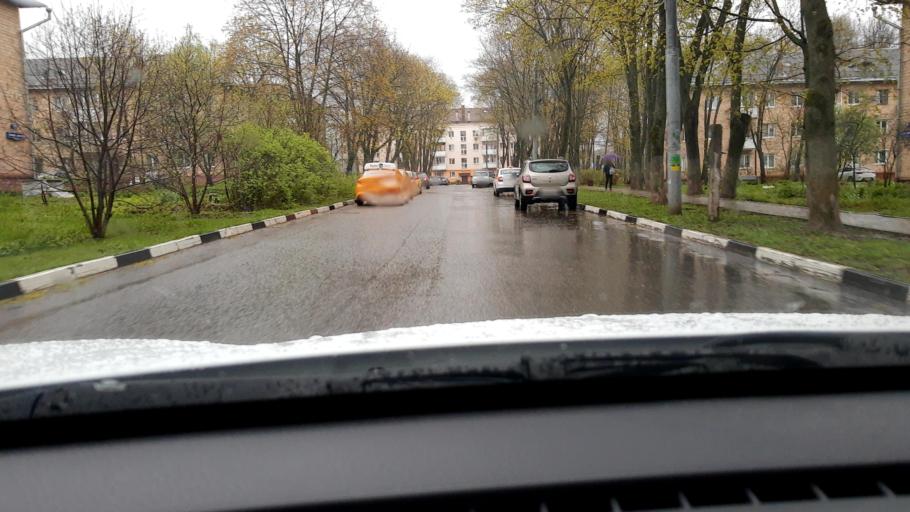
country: RU
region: Moskovskaya
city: Gorki-Leninskiye
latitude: 55.5071
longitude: 37.7782
